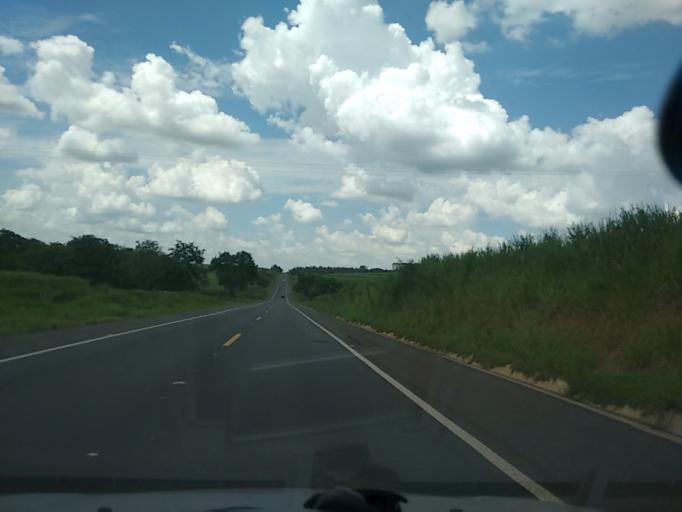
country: BR
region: Sao Paulo
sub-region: Osvaldo Cruz
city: Osvaldo Cruz
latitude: -21.8612
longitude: -50.8465
